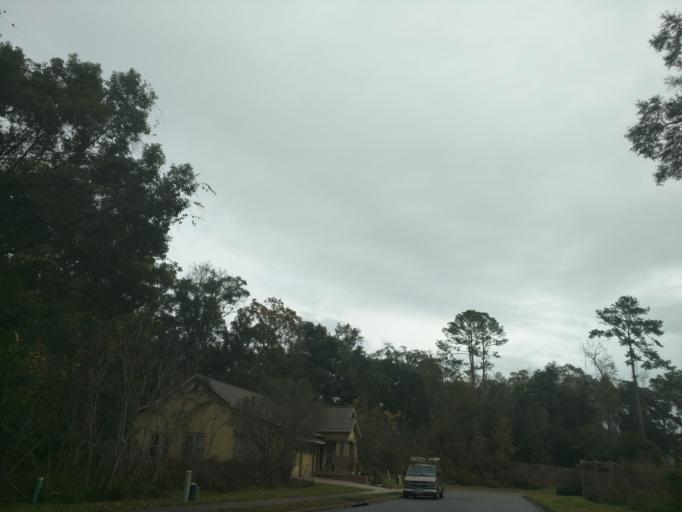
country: US
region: Florida
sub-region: Leon County
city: Tallahassee
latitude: 30.4632
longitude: -84.2333
